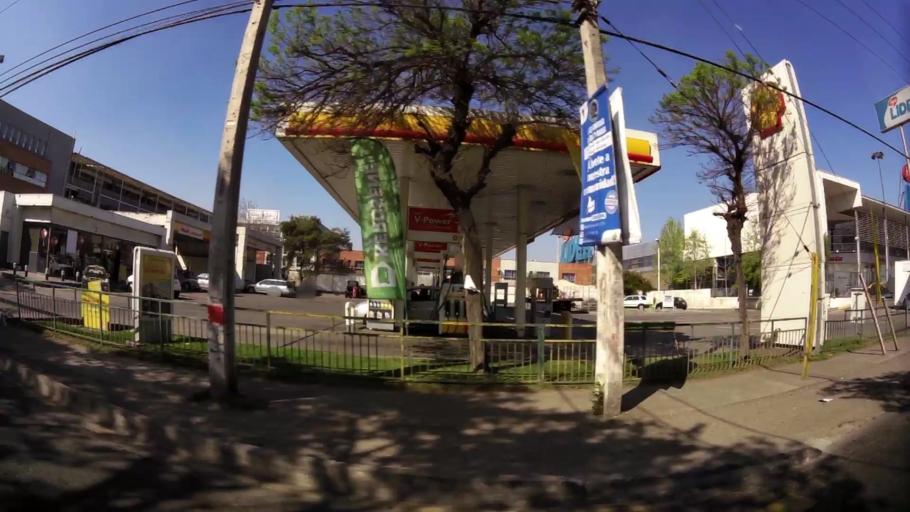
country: CL
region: Santiago Metropolitan
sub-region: Provincia de Santiago
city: Lo Prado
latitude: -33.5019
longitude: -70.7573
